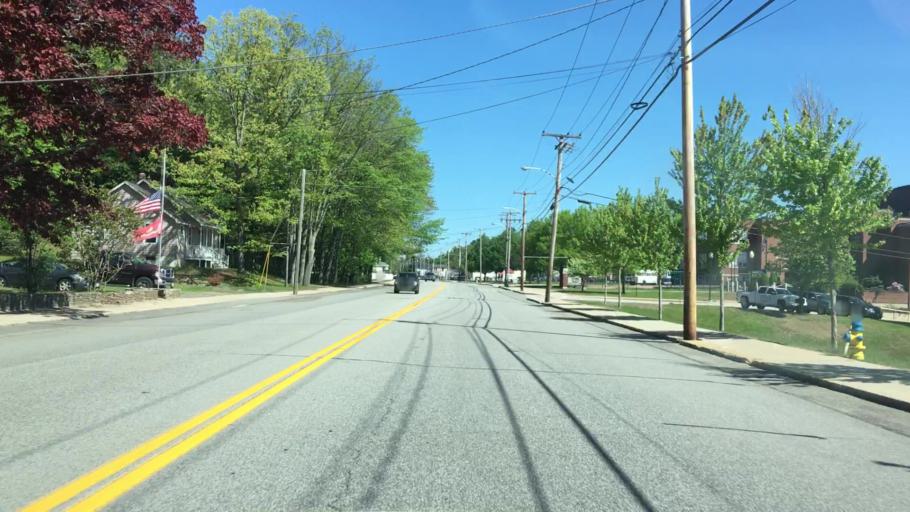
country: US
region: Maine
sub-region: York County
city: Springvale
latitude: 43.4510
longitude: -70.7879
